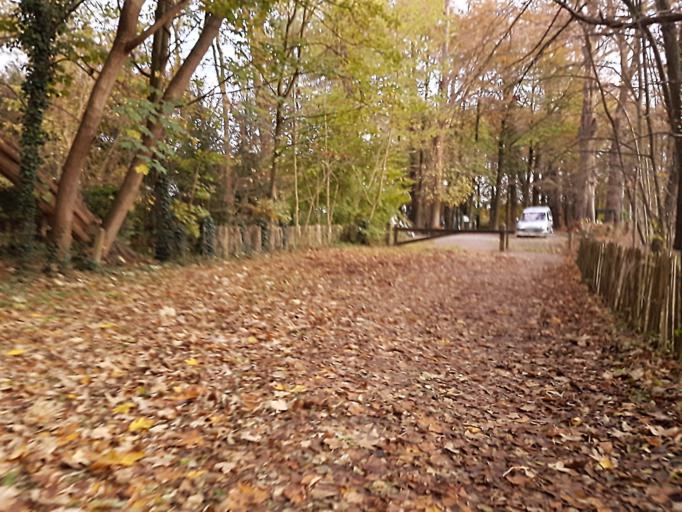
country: BE
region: Flanders
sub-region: Provincie Antwerpen
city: Ranst
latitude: 51.1957
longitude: 4.5578
